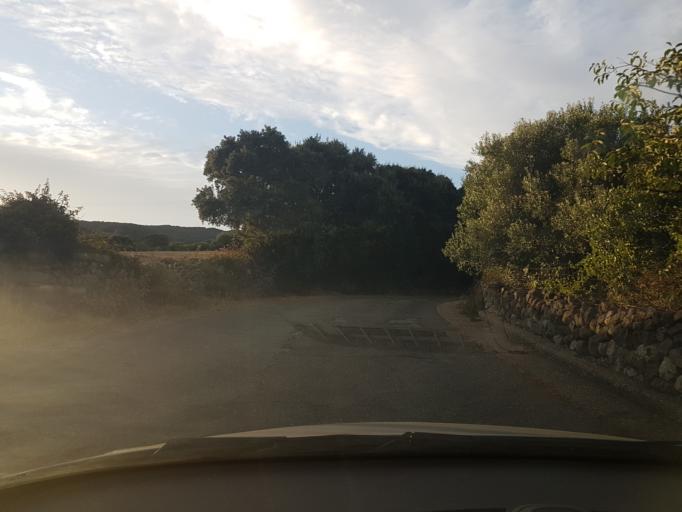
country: IT
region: Sardinia
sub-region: Provincia di Oristano
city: Seneghe
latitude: 40.1048
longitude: 8.6220
